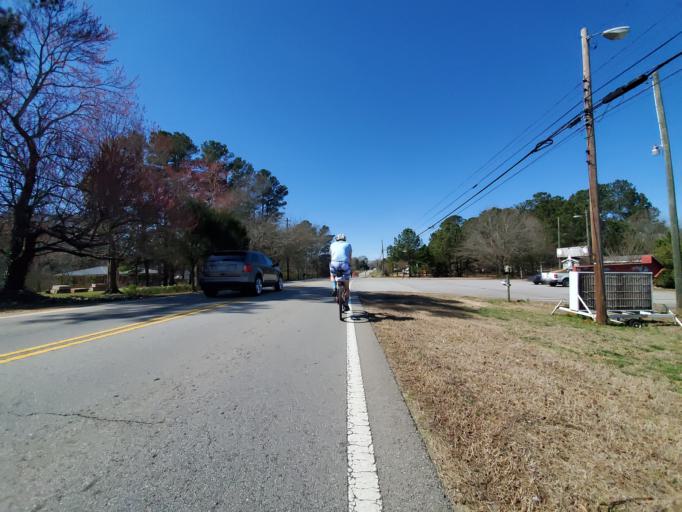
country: US
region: Georgia
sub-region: Barrow County
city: Winder
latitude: 33.9978
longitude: -83.7021
